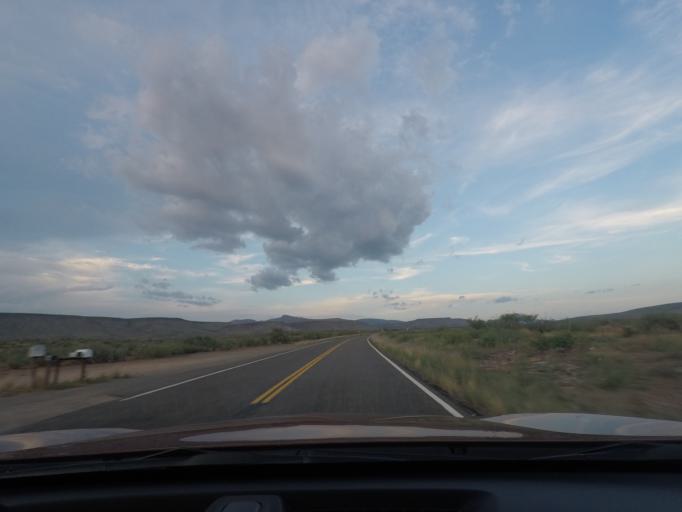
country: US
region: Arizona
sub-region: Yavapai County
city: Bagdad
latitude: 34.4792
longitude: -112.8814
